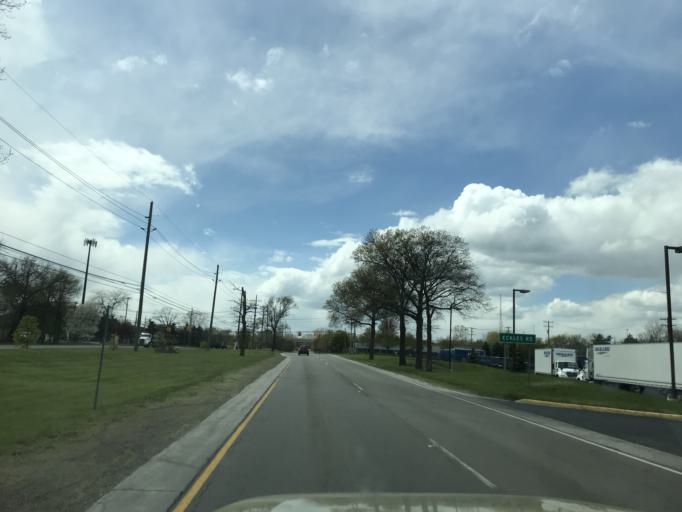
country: US
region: Michigan
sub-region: Wayne County
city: Plymouth
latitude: 42.3821
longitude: -83.4292
